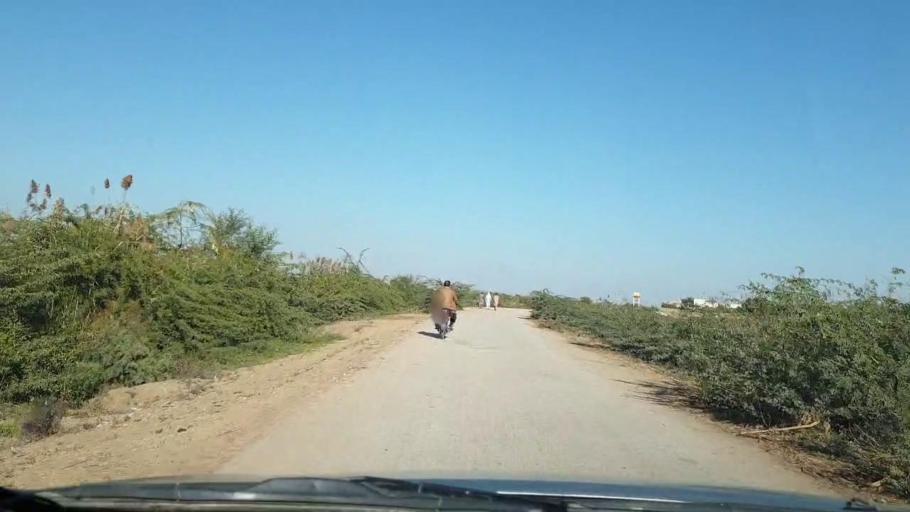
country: PK
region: Sindh
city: Berani
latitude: 25.8168
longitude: 68.9456
